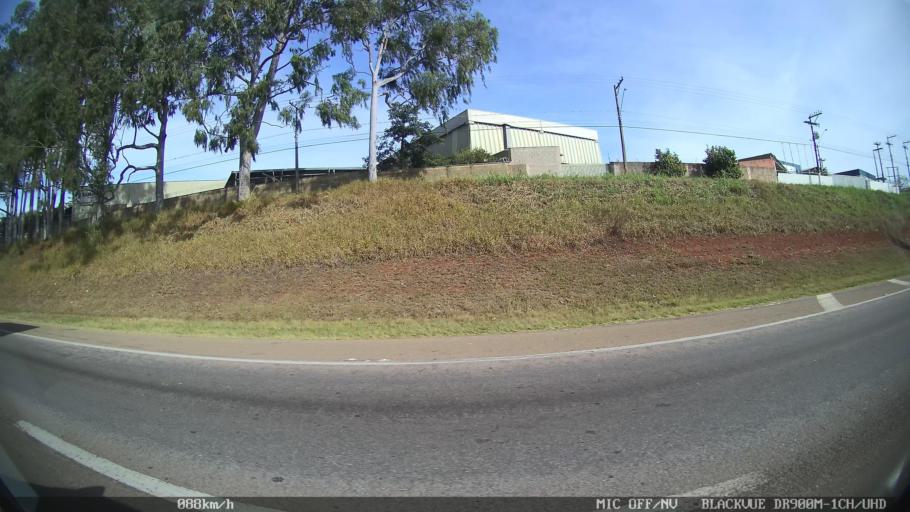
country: BR
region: Sao Paulo
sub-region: Piracicaba
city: Piracicaba
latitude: -22.7673
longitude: -47.5952
